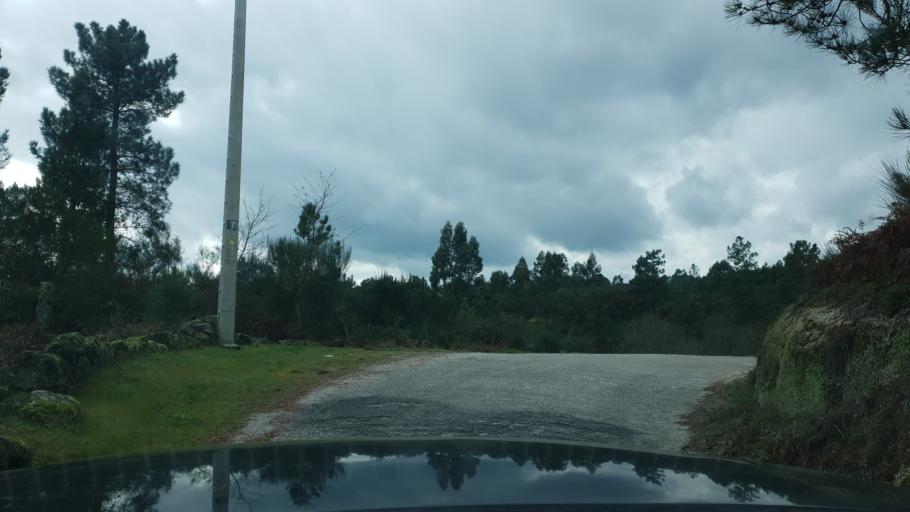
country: PT
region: Viseu
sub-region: Castro Daire
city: Castro Daire
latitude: 40.8730
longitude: -7.9792
